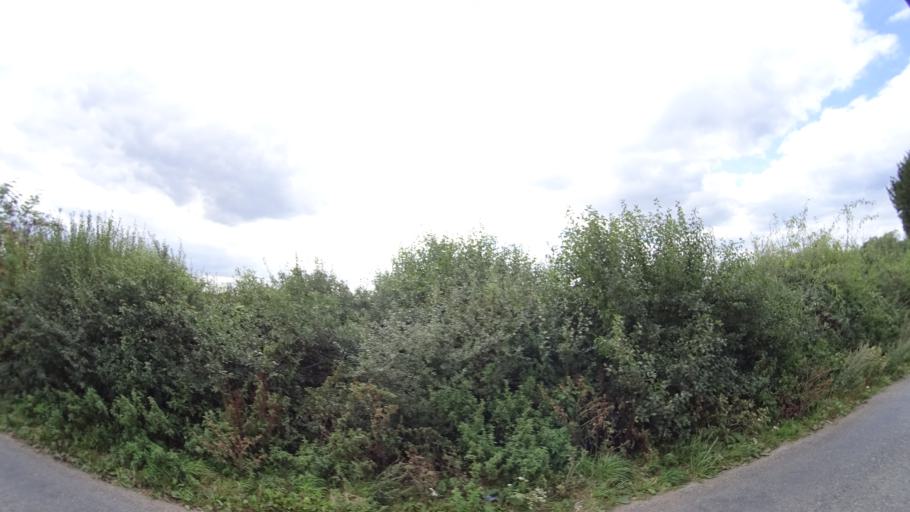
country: GB
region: England
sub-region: Wiltshire
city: Tidworth
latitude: 51.1883
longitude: -1.6561
